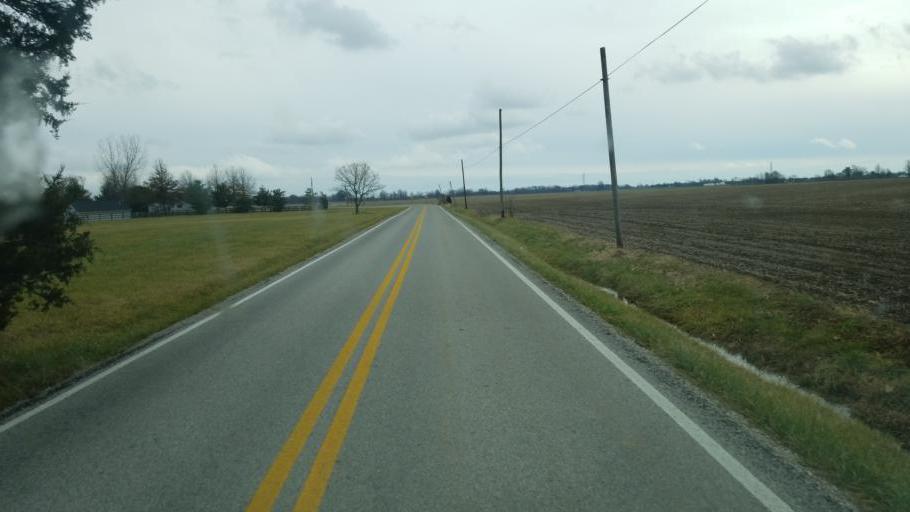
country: US
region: Ohio
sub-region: Delaware County
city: Delaware
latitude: 40.2789
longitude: -83.0310
